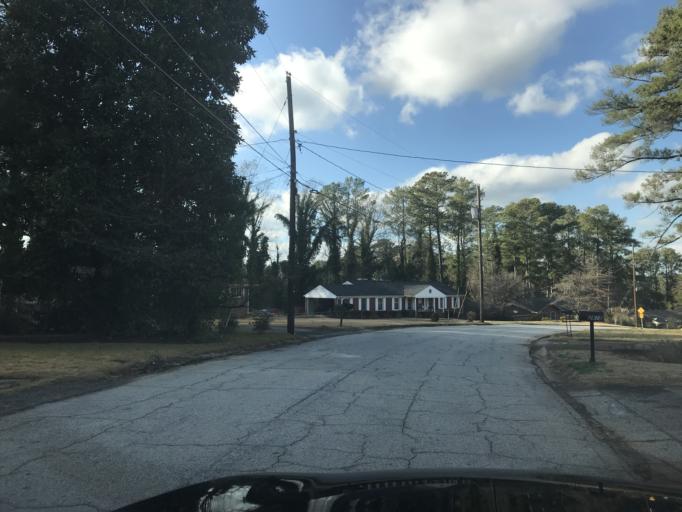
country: US
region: Georgia
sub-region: Fulton County
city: College Park
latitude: 33.6396
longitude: -84.4747
